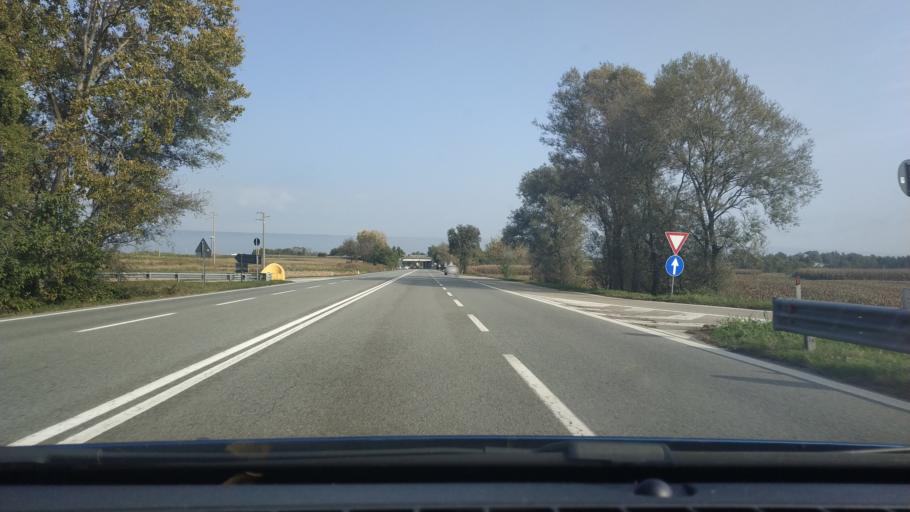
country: IT
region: Piedmont
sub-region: Provincia di Torino
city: Romano Canavese
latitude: 45.4175
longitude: 7.8851
